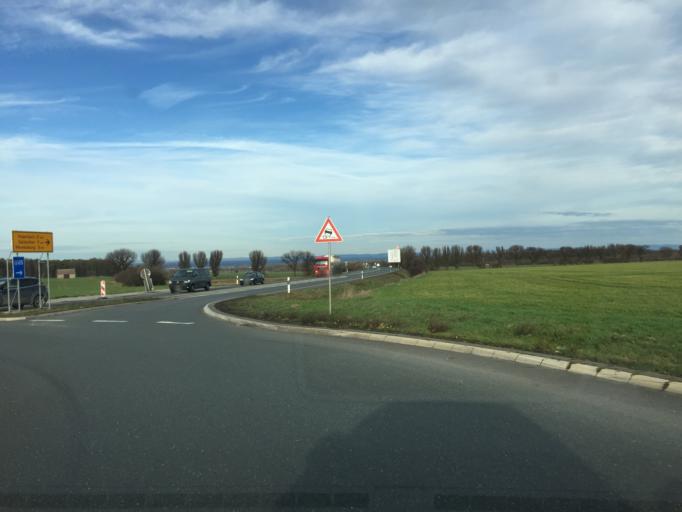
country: DE
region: North Rhine-Westphalia
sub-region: Regierungsbezirk Detmold
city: Buren
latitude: 51.5979
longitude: 8.5856
